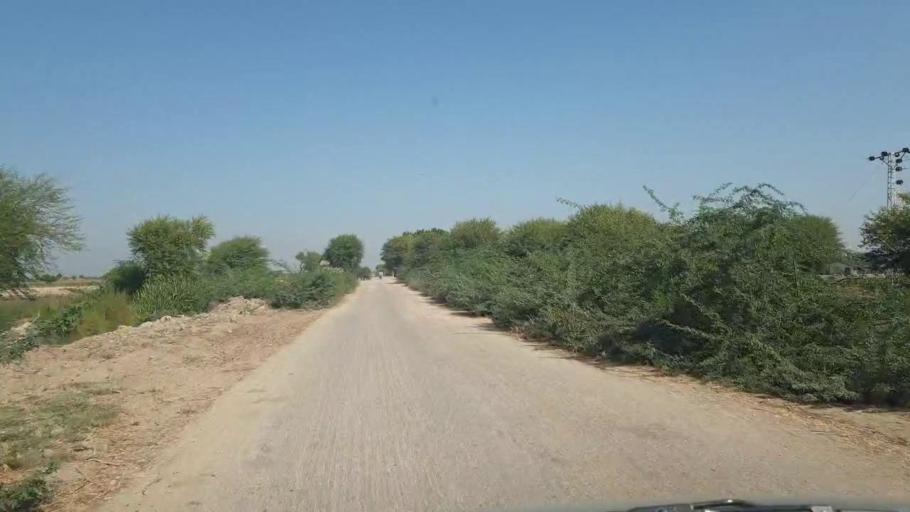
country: PK
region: Sindh
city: Tando Bago
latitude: 24.8193
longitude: 68.9848
